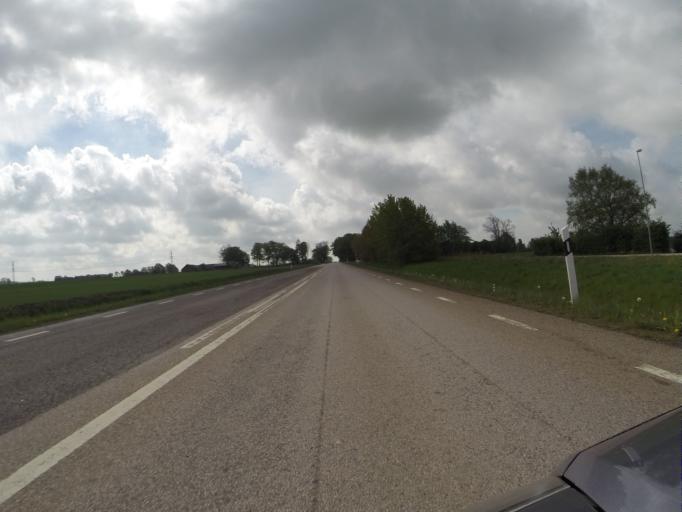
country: SE
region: Skane
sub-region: Landskrona
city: Asmundtorp
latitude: 55.9776
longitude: 12.9369
